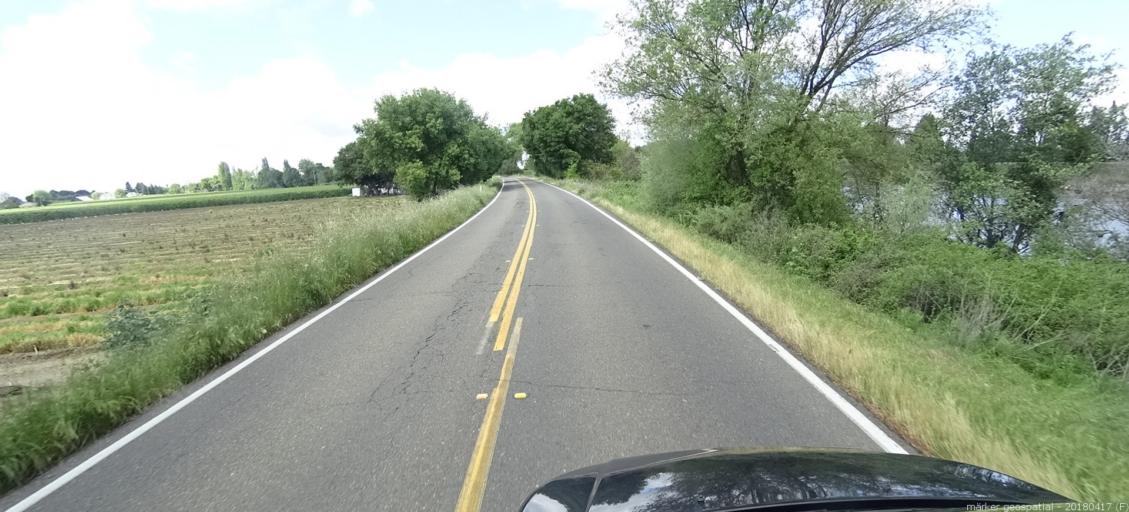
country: US
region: California
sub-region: Sacramento County
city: Walnut Grove
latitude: 38.2409
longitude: -121.5489
